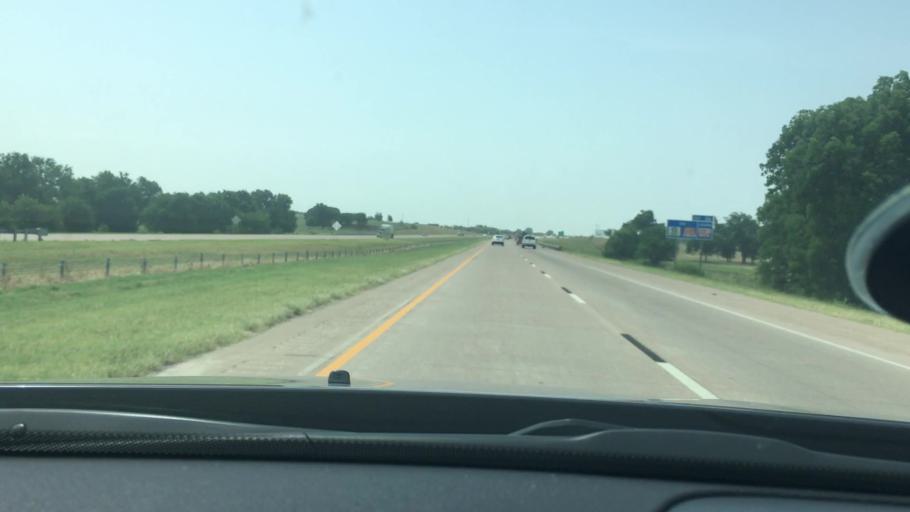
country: US
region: Oklahoma
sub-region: Garvin County
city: Wynnewood
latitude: 34.6649
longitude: -97.2230
